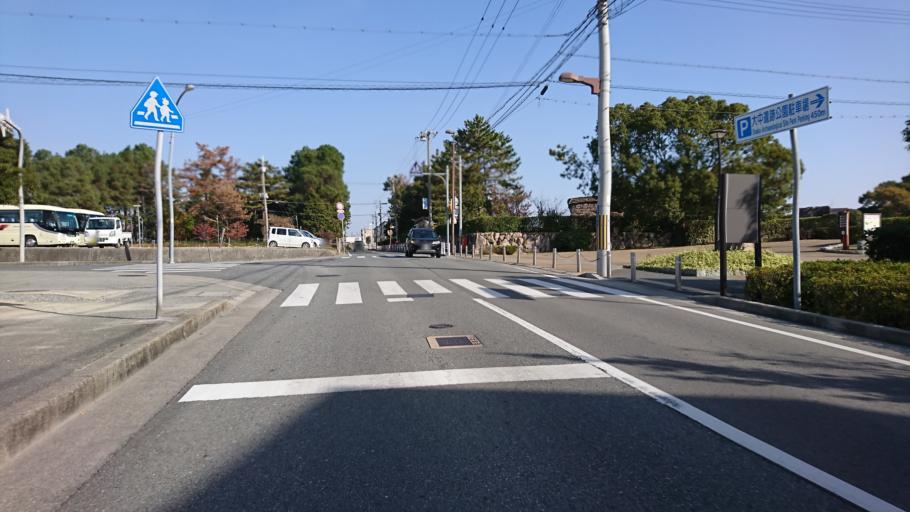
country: JP
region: Hyogo
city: Kakogawacho-honmachi
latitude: 34.7273
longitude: 134.8756
